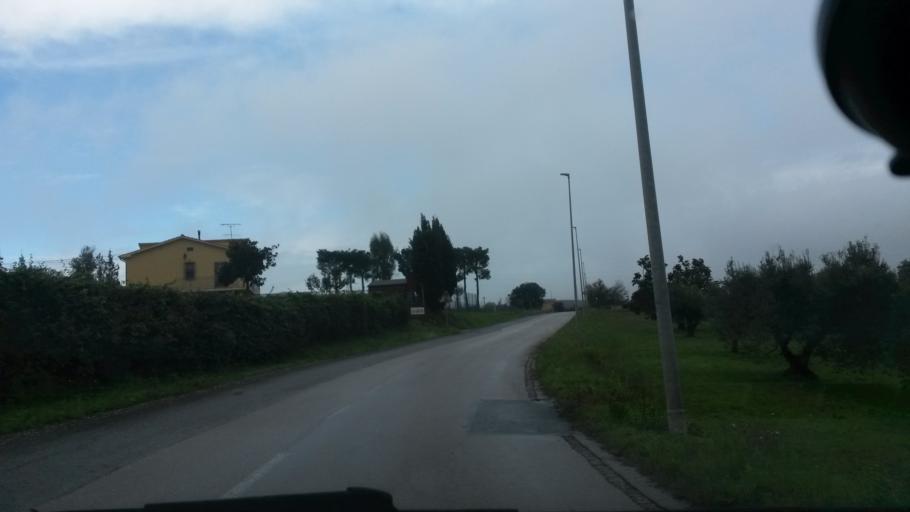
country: IT
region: Tuscany
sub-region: Provincia di Livorno
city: Rosignano Marittimo
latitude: 43.4153
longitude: 10.4636
